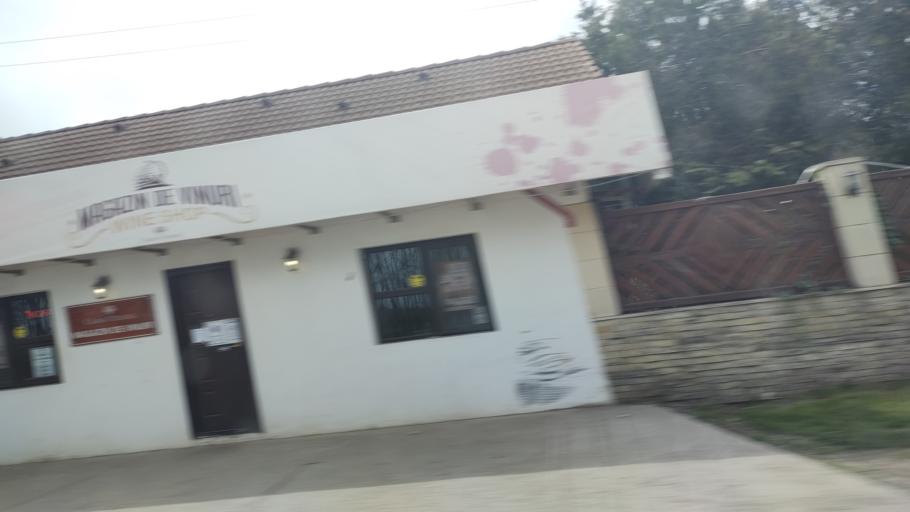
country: RO
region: Constanta
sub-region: Comuna Cobadin
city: Viisoara
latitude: 44.0779
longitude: 28.1782
